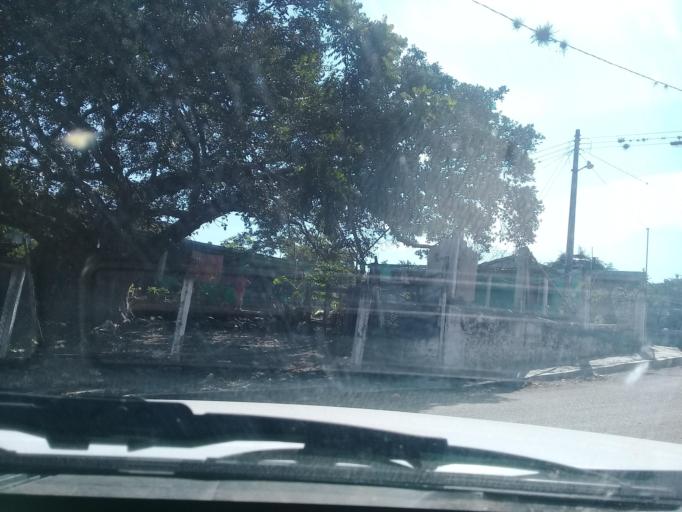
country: MX
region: Veracruz
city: Rinconada
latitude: 19.4387
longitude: -96.5623
